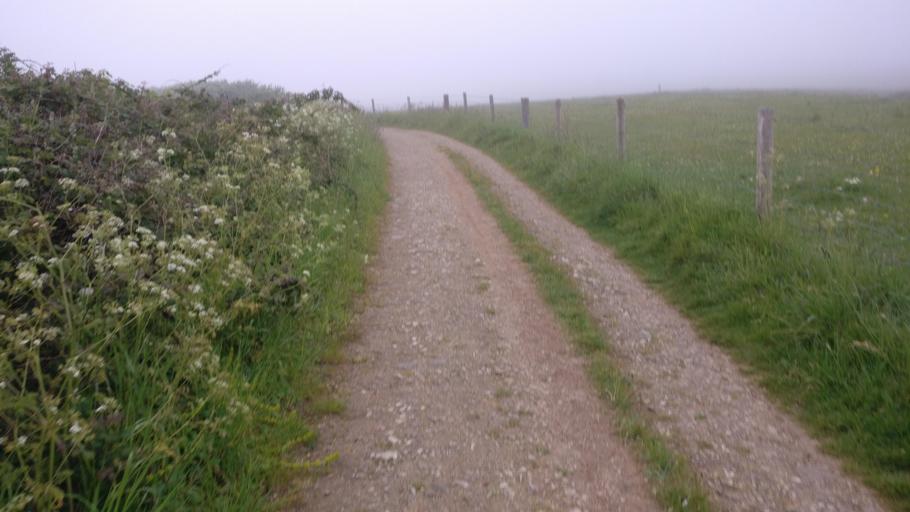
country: GB
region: England
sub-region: Dorset
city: Swanage
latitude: 50.6020
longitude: -2.0176
